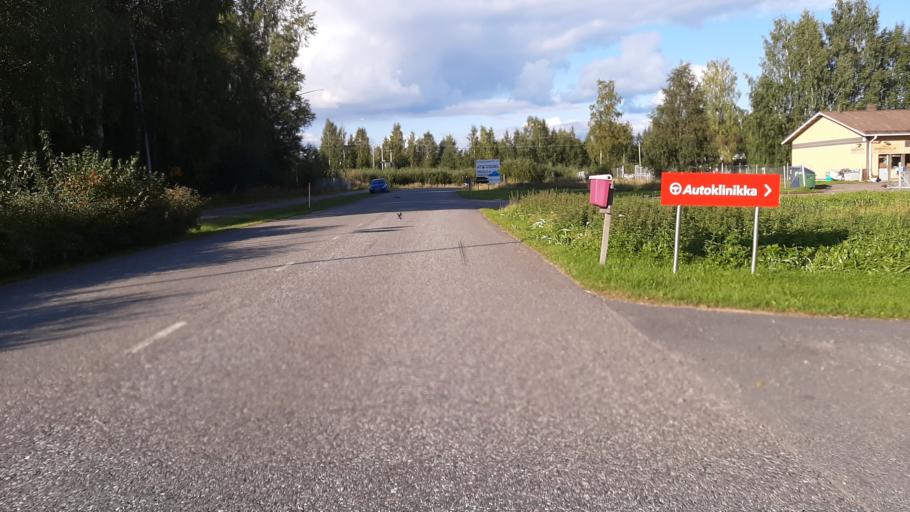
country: FI
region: North Karelia
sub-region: Joensuu
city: Joensuu
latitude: 62.6290
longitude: 29.8020
